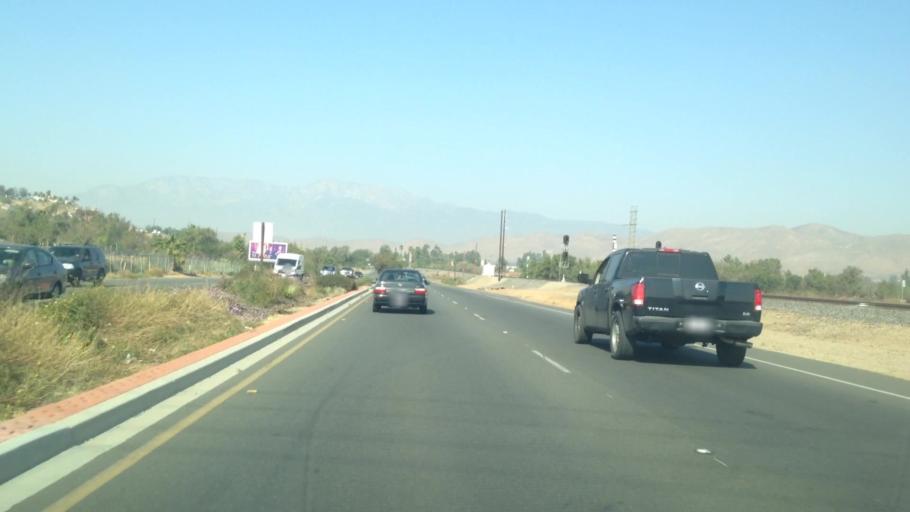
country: US
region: California
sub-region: Riverside County
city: Pedley
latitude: 33.9866
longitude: -117.4796
